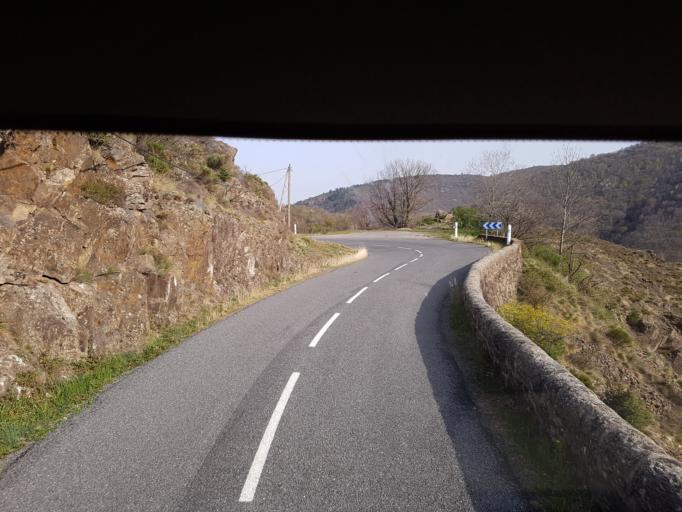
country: FR
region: Languedoc-Roussillon
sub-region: Departement du Gard
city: Branoux-les-Taillades
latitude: 44.3336
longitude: 3.8776
